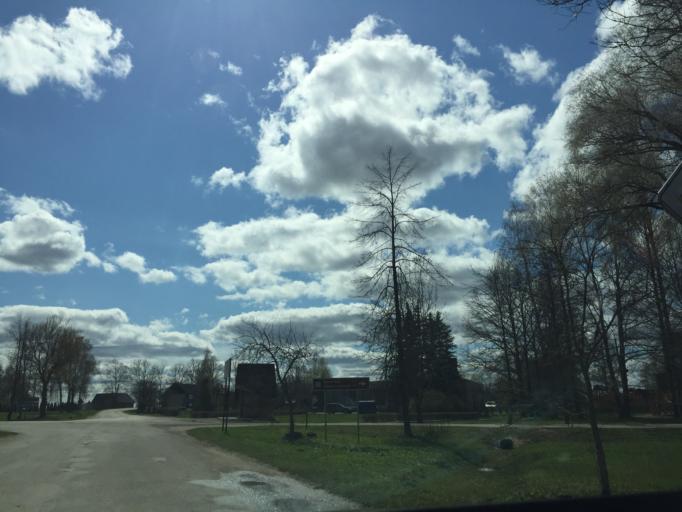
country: LV
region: Vilanu
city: Vilani
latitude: 56.7343
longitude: 27.0670
